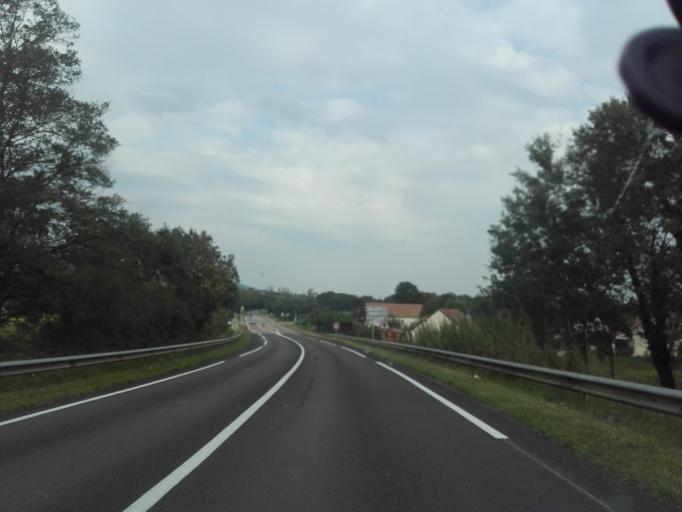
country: FR
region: Bourgogne
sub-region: Departement de Saone-et-Loire
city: Chagny
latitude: 46.9056
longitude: 4.7098
